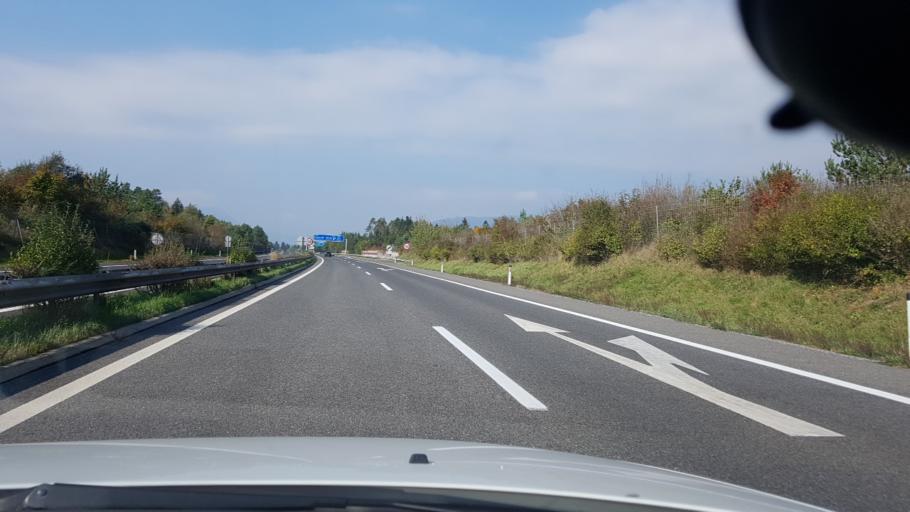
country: AT
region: Carinthia
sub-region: Politischer Bezirk Villach Land
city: Wernberg
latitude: 46.6128
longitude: 13.9171
